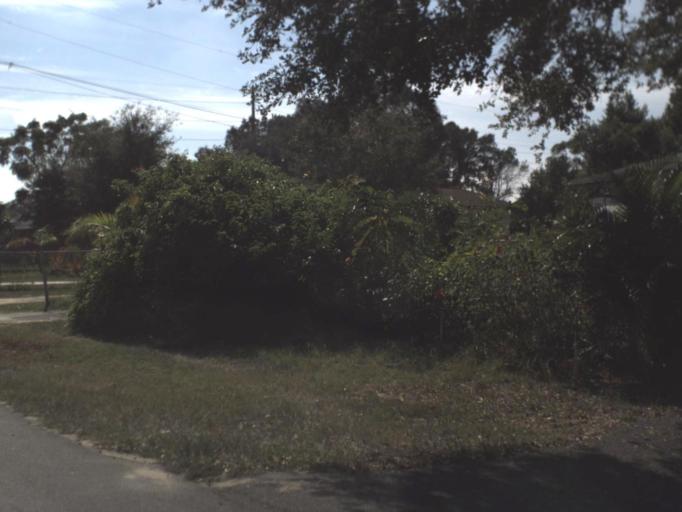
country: US
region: Florida
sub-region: Highlands County
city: Sebring
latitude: 27.5103
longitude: -81.4440
